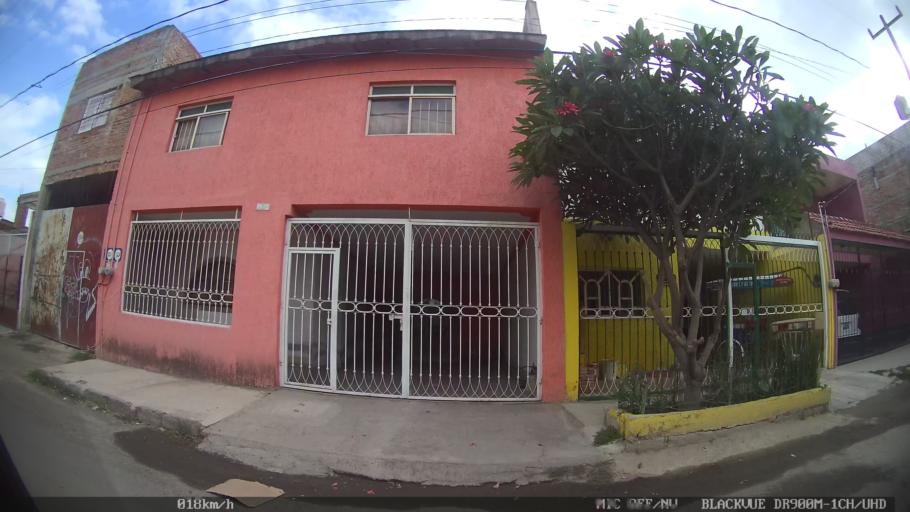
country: MX
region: Jalisco
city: Tonala
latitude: 20.6651
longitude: -103.2365
